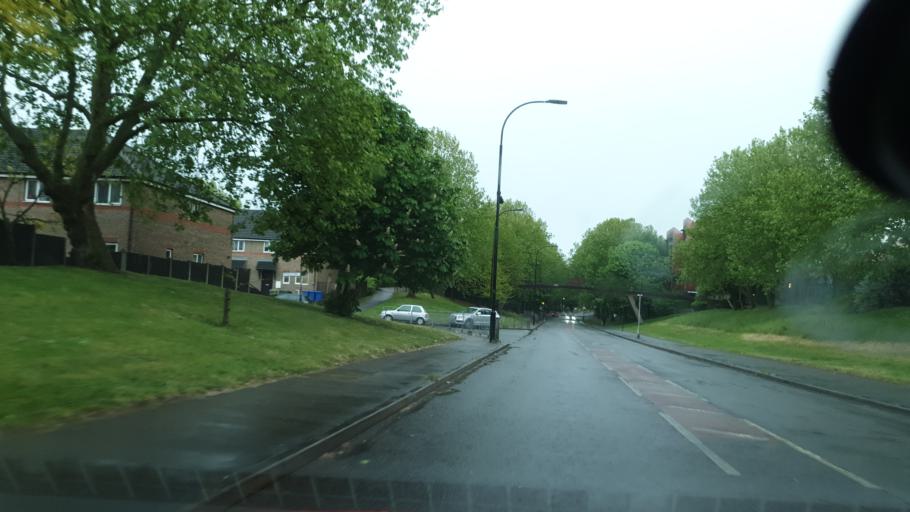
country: GB
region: England
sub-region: Greater London
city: Poplar
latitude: 51.5024
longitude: -0.0357
